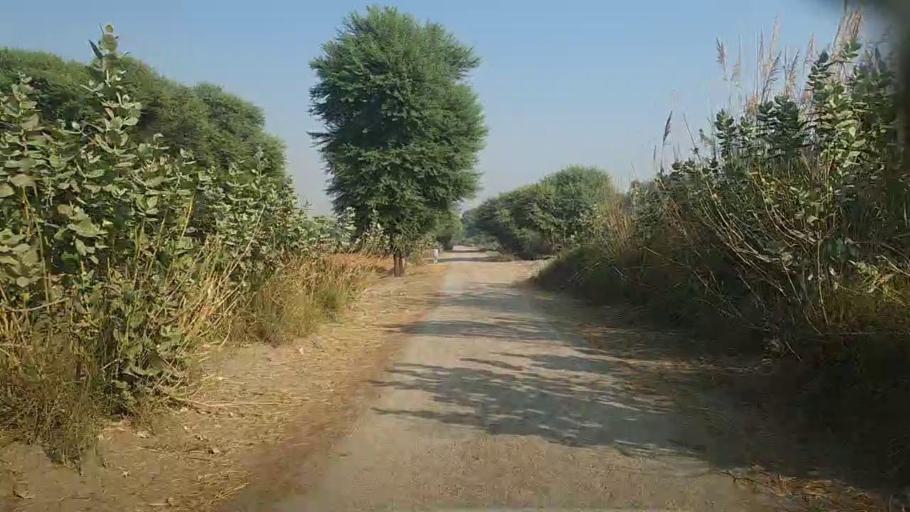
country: PK
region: Sindh
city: Karaundi
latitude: 26.7660
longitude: 68.4780
